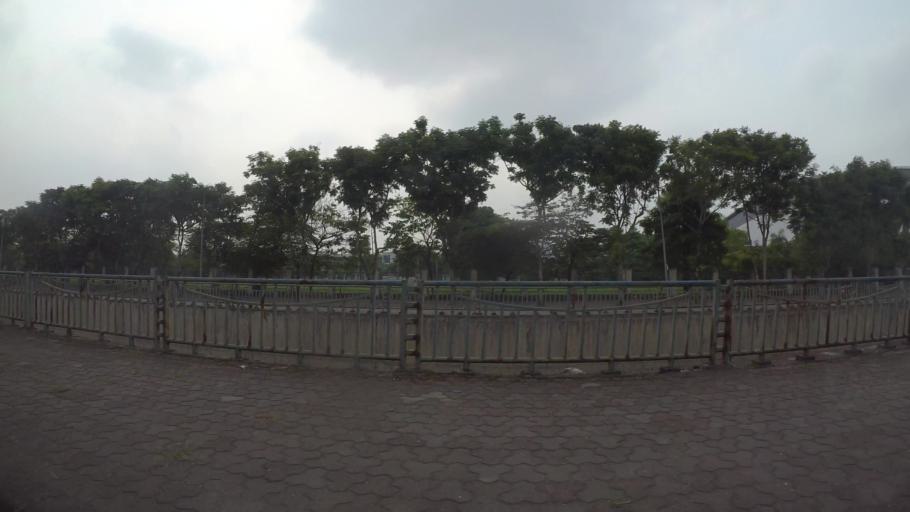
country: VN
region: Ha Noi
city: Cau Dien
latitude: 21.0273
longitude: 105.7635
